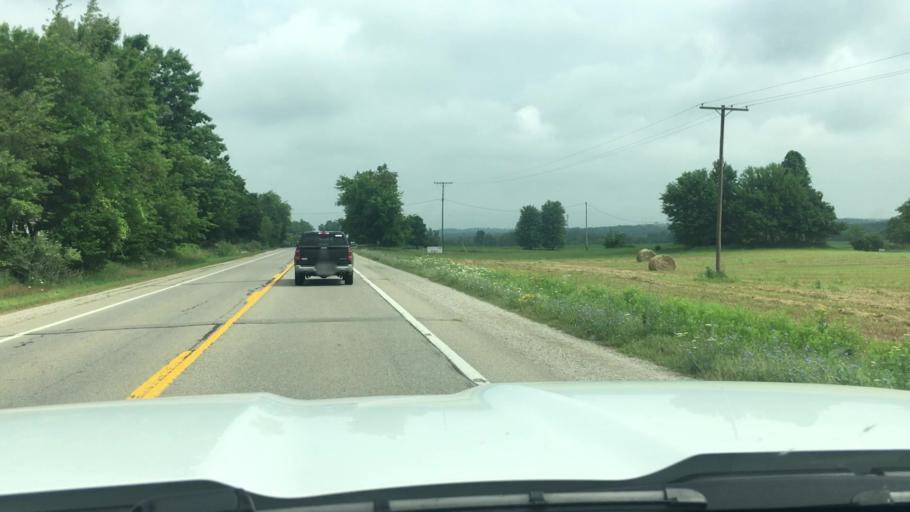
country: US
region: Michigan
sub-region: Sanilac County
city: Brown City
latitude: 43.1392
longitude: -83.0738
